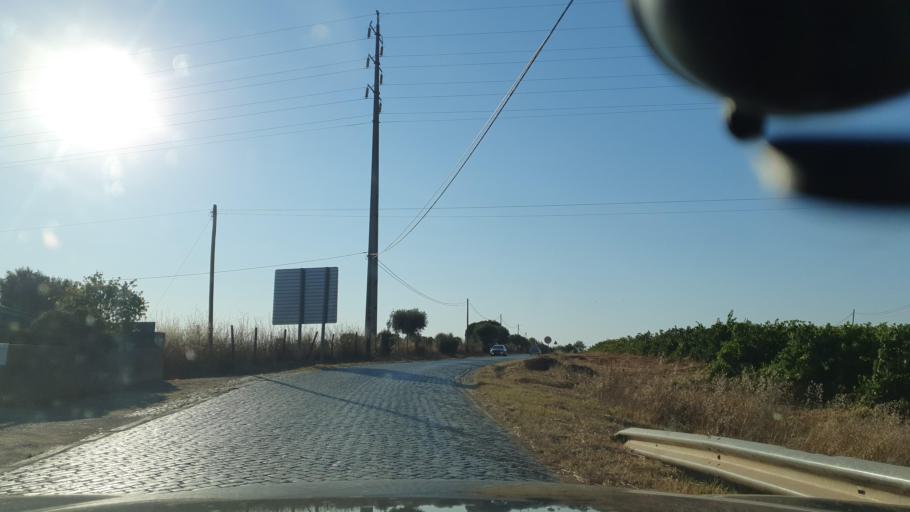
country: PT
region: Evora
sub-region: Estremoz
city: Estremoz
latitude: 38.8473
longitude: -7.6054
